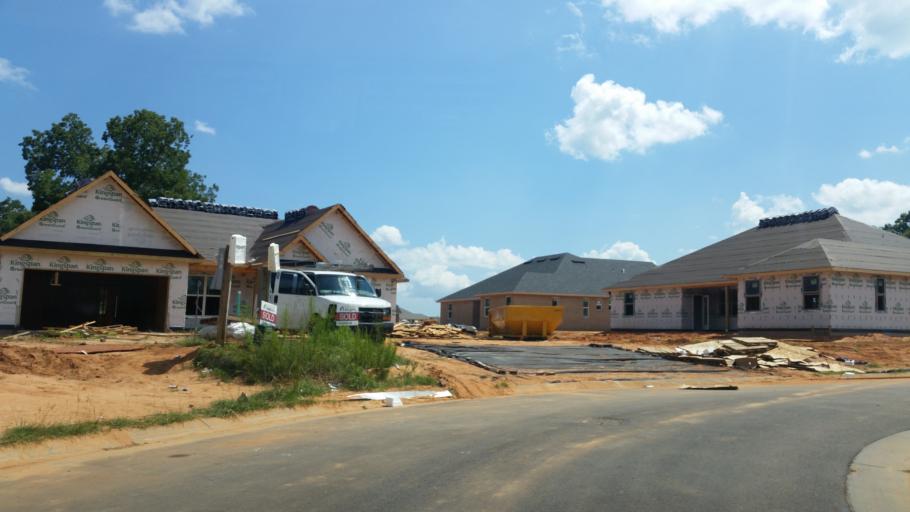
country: US
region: Florida
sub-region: Escambia County
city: Cantonment
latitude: 30.5542
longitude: -87.3693
